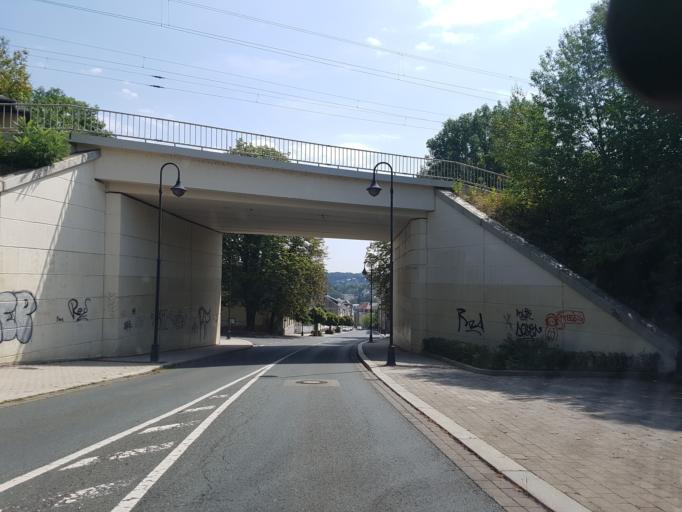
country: DE
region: Saxony
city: Waldheim
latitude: 51.0742
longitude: 13.0141
